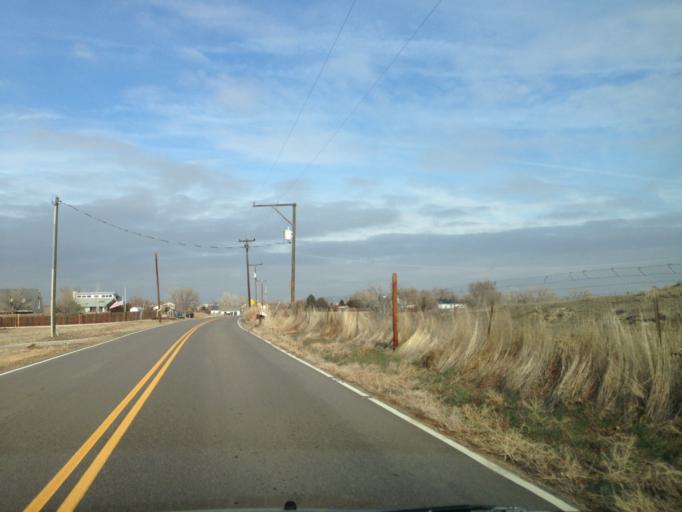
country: US
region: Colorado
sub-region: Boulder County
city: Lafayette
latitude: 39.9955
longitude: -105.0606
